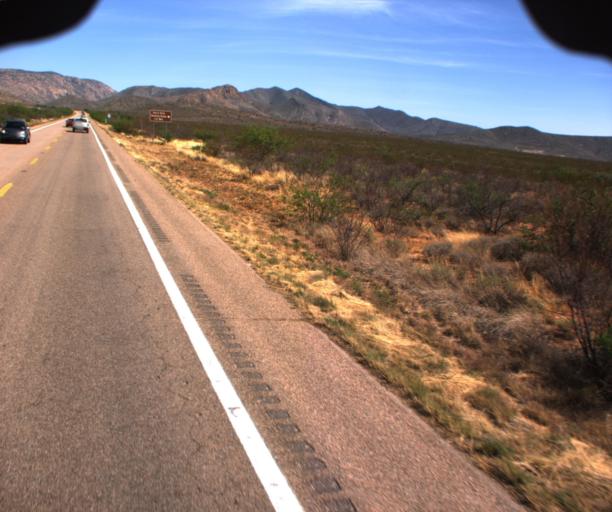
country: US
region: Arizona
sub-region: Cochise County
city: Bisbee
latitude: 31.5305
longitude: -110.0558
